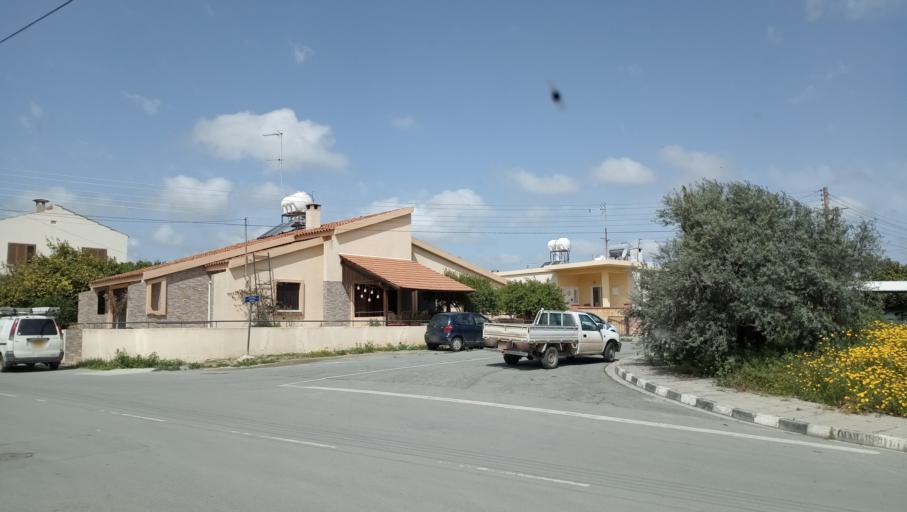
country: CY
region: Lefkosia
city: Dali
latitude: 35.0247
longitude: 33.4277
